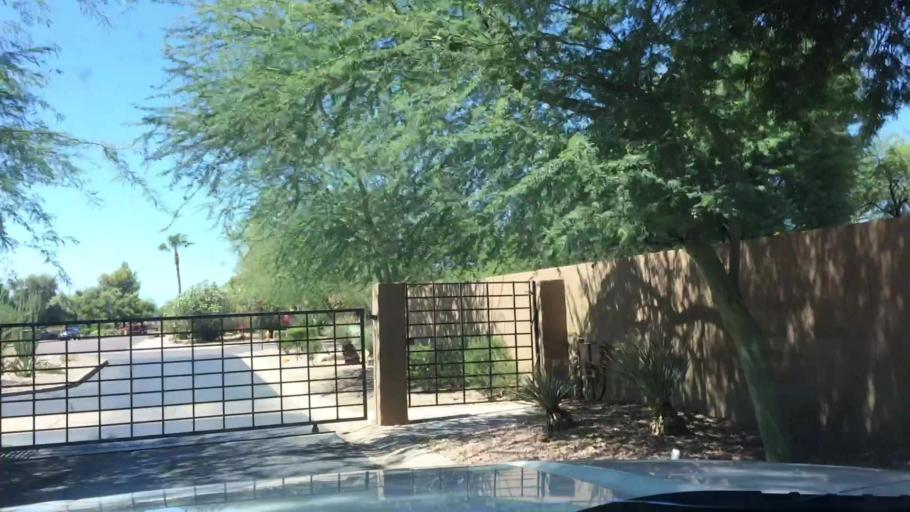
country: US
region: Arizona
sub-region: Maricopa County
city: Scottsdale
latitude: 33.5932
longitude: -111.8734
